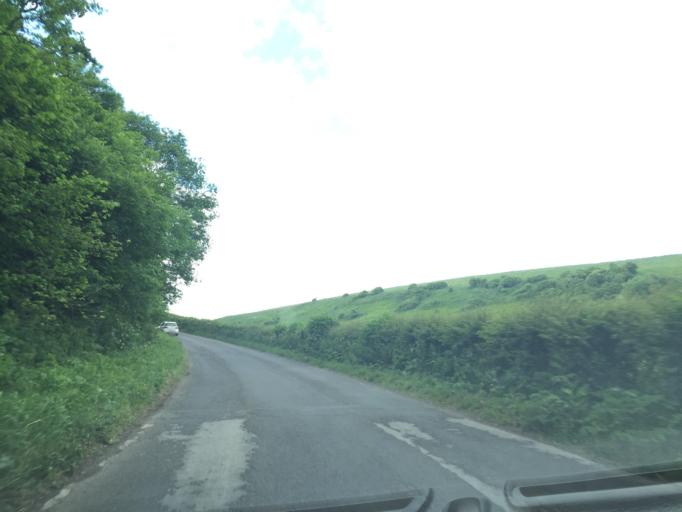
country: GB
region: England
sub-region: Dorset
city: Wool
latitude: 50.6470
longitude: -2.2675
